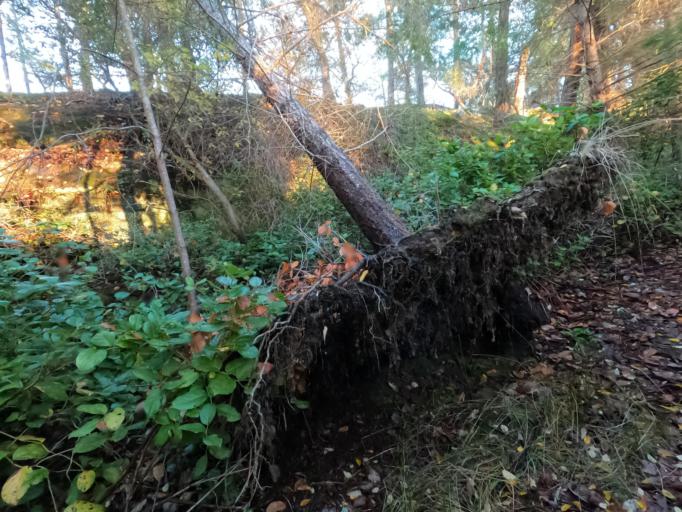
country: CA
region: British Columbia
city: North Cowichan
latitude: 48.9517
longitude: -123.5669
